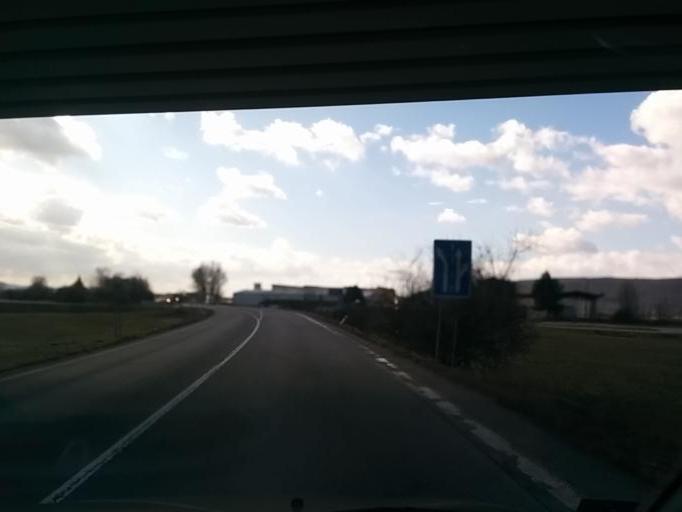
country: SK
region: Trenciansky
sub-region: Okres Nove Mesto nad Vahom
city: Nove Mesto nad Vahom
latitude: 48.8117
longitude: 17.8883
